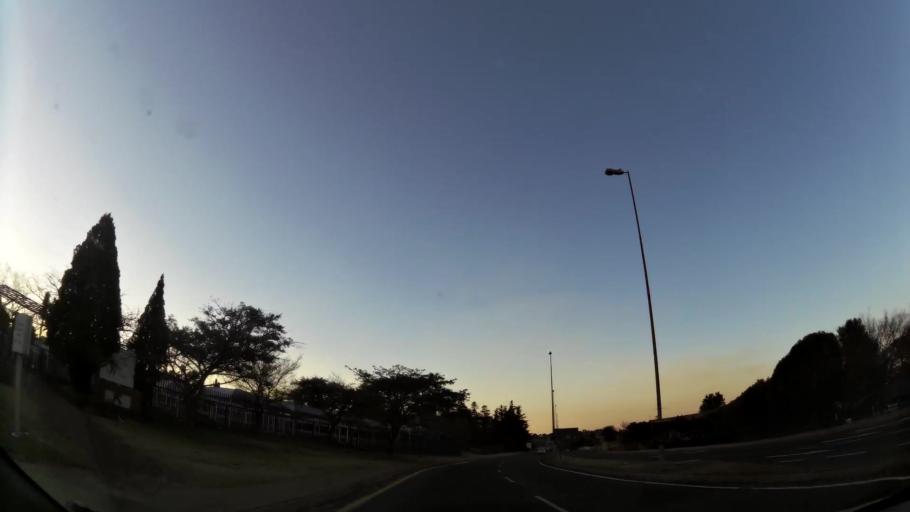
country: ZA
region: Gauteng
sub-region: City of Johannesburg Metropolitan Municipality
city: Roodepoort
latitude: -26.1566
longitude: 27.9005
